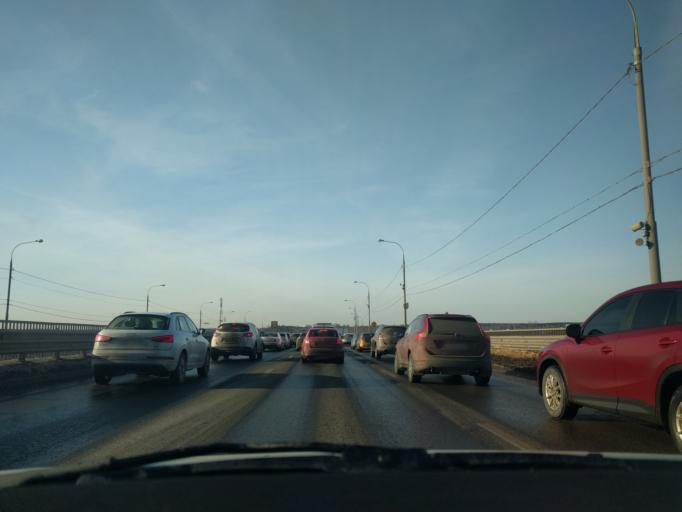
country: RU
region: Moskovskaya
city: Sheremet'yevskiy
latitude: 55.9728
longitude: 37.5276
